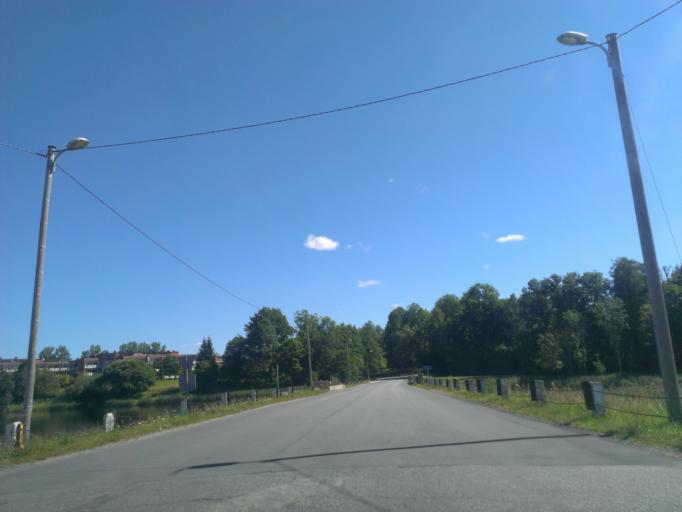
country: LV
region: Malpils
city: Malpils
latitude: 57.0110
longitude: 24.9467
